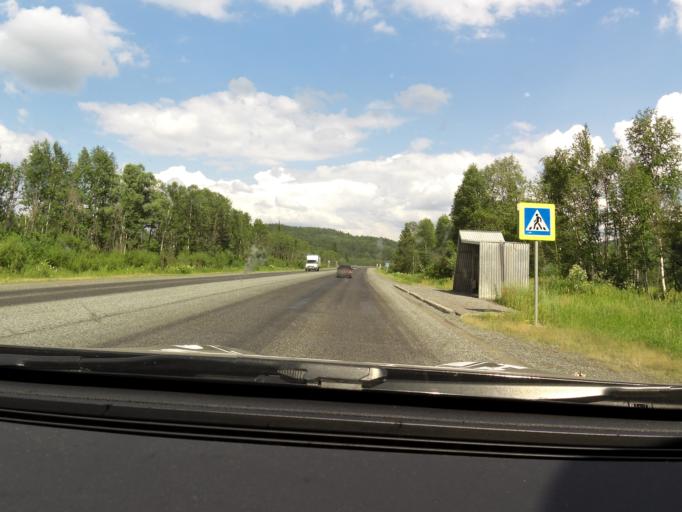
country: RU
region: Sverdlovsk
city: Arti
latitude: 56.7945
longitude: 58.6158
